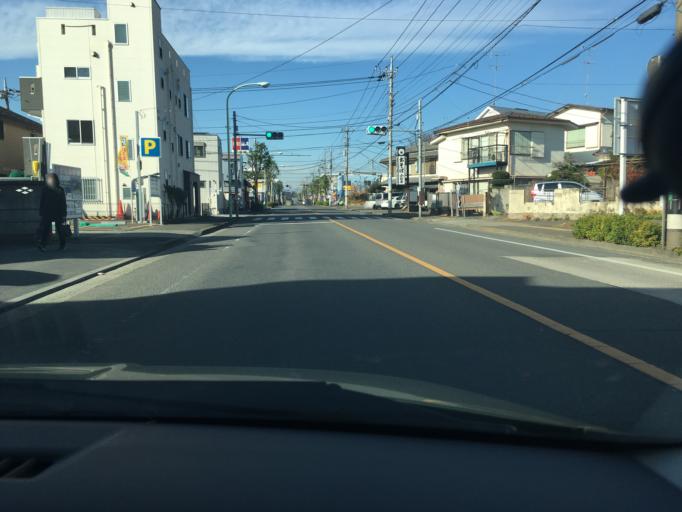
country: JP
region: Tokyo
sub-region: Machida-shi
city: Machida
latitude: 35.5668
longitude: 139.4185
